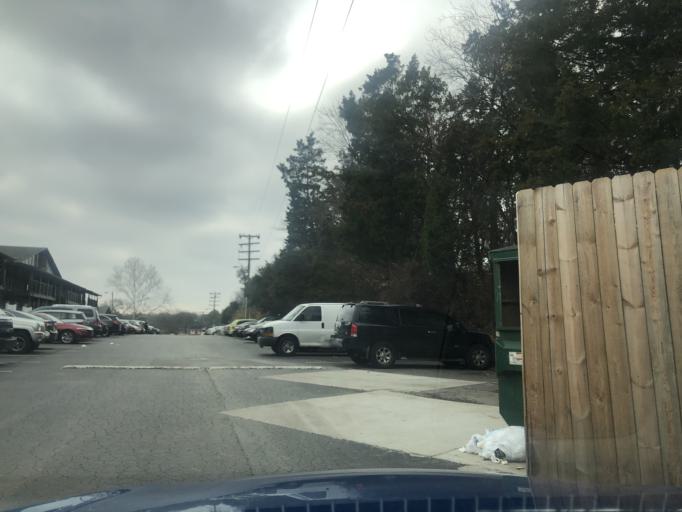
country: US
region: Tennessee
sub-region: Davidson County
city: Oak Hill
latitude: 36.0890
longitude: -86.7040
